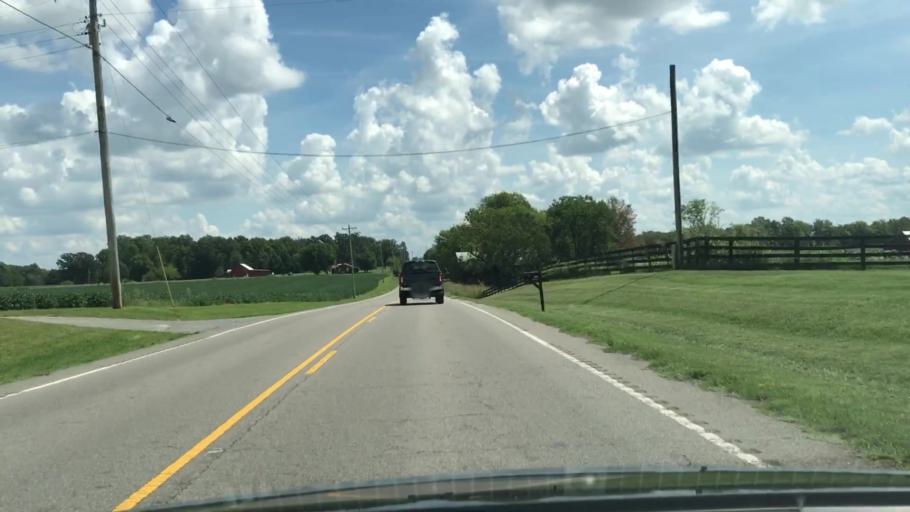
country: US
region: Tennessee
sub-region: Robertson County
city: Cross Plains
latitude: 36.5539
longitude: -86.7861
